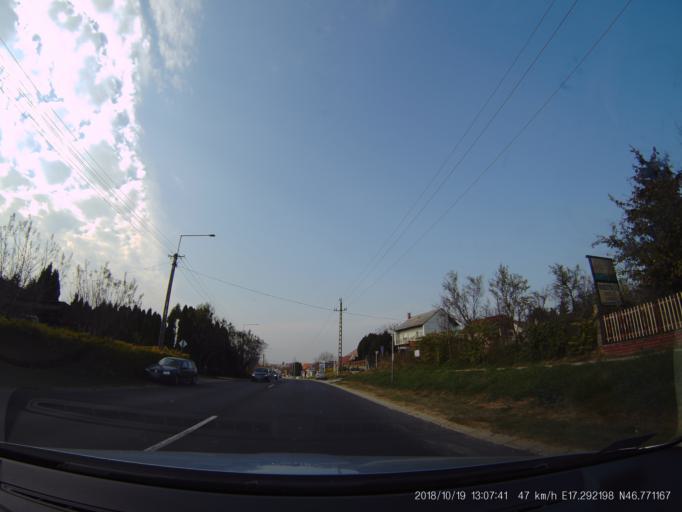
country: HU
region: Zala
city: Gyenesdias
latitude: 46.7712
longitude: 17.2921
